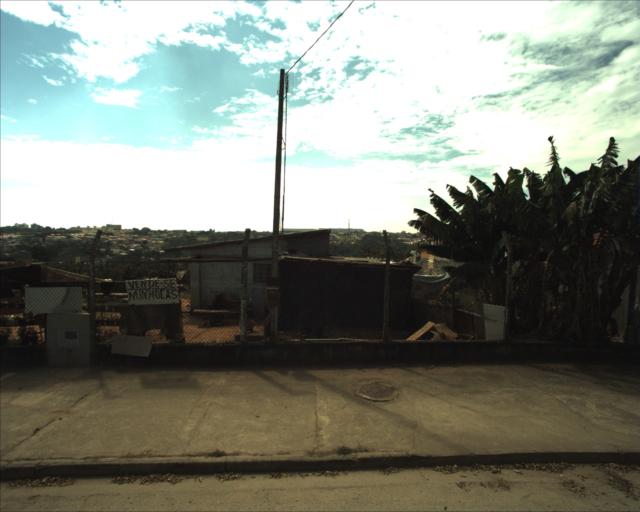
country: BR
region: Sao Paulo
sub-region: Sorocaba
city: Sorocaba
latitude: -23.4866
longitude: -47.5005
